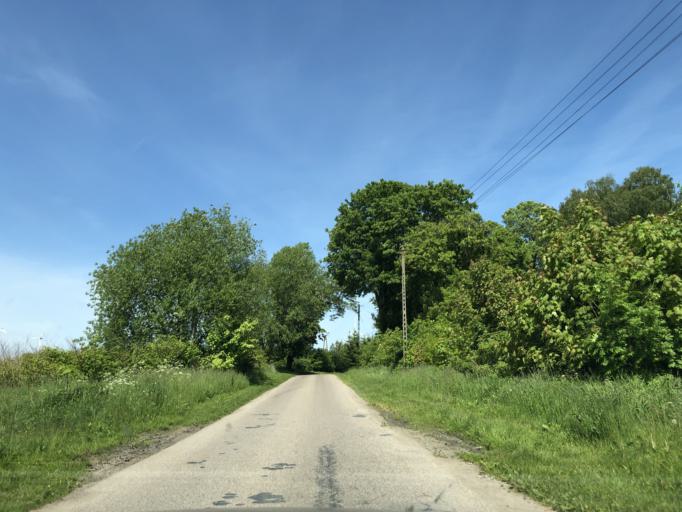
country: PL
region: West Pomeranian Voivodeship
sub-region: Powiat kolobrzeski
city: Goscino
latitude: 54.0465
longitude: 15.7269
